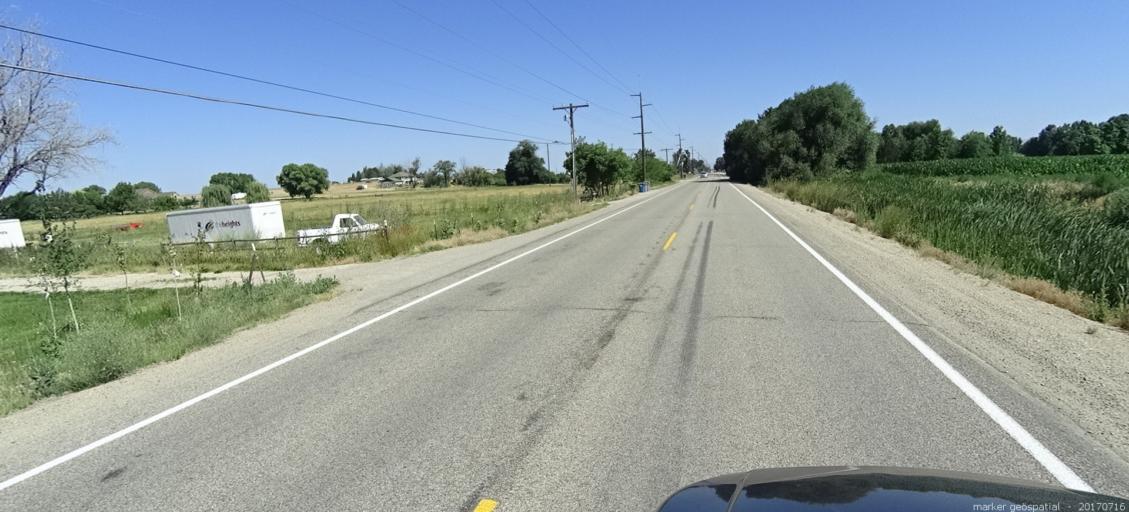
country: US
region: Idaho
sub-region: Ada County
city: Kuna
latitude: 43.5248
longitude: -116.3344
